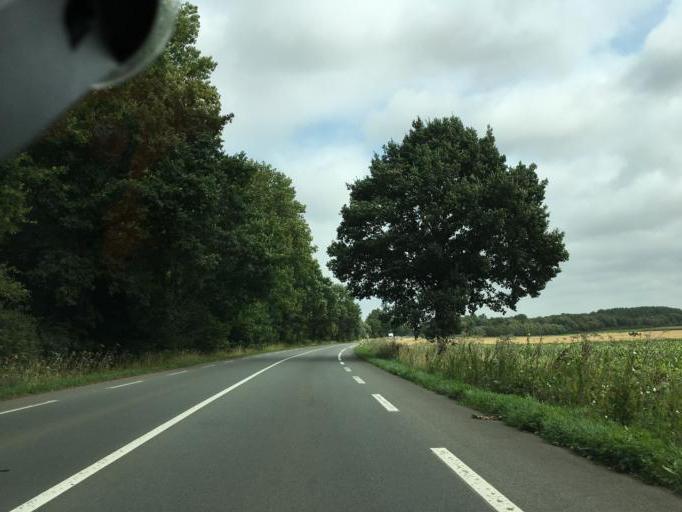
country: FR
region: Nord-Pas-de-Calais
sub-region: Departement du Pas-de-Calais
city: Pernes
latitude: 50.4228
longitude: 2.4251
